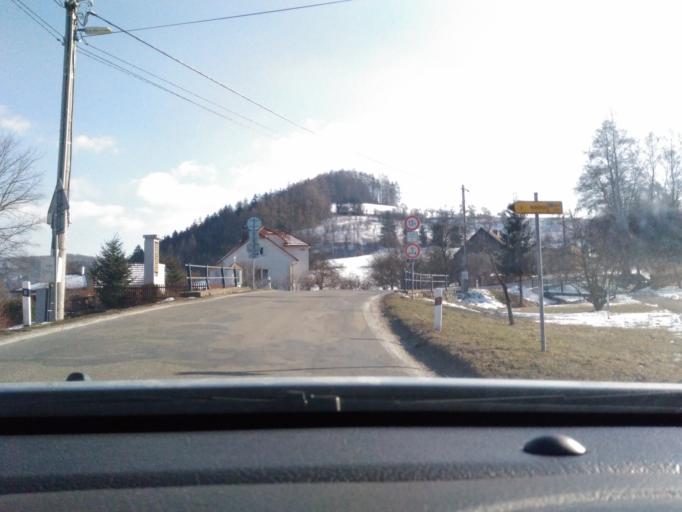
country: CZ
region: South Moravian
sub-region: Okres Brno-Venkov
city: Nedvedice
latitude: 49.4826
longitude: 16.3350
